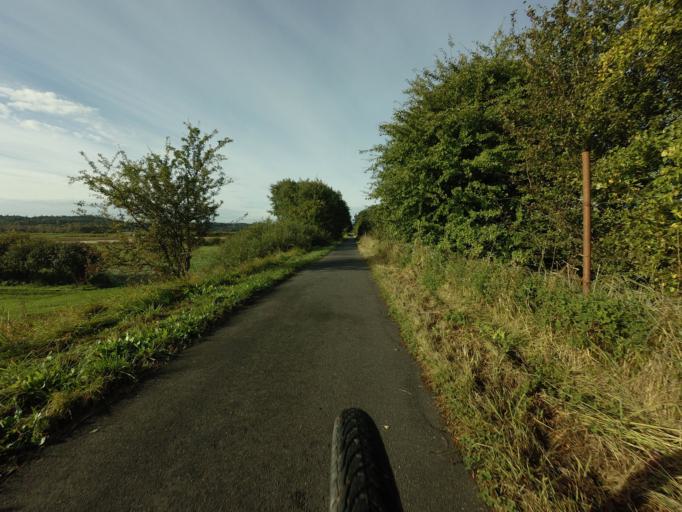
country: DK
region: Central Jutland
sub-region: Viborg Kommune
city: Bjerringbro
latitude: 56.4428
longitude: 9.5658
